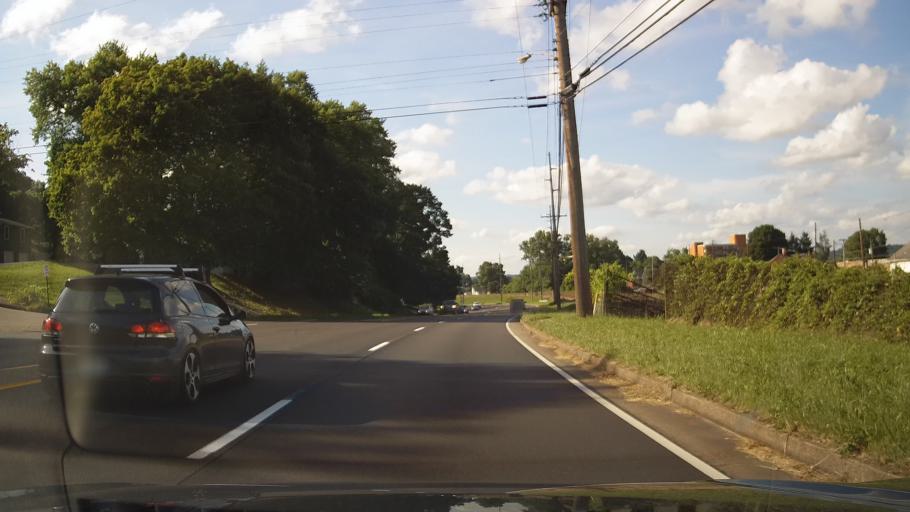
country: US
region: Kentucky
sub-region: Boyd County
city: Catlettsburg
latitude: 38.4157
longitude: -82.5996
